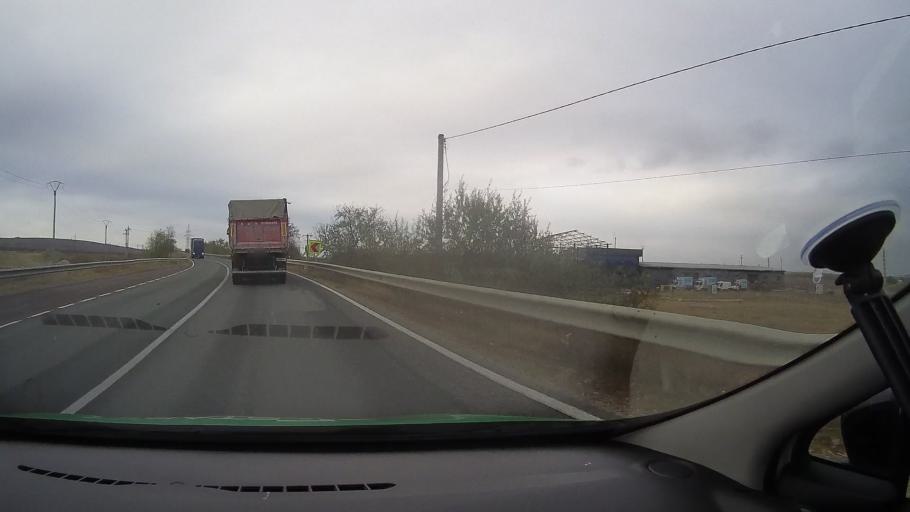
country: RO
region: Constanta
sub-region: Comuna Poarta Alba
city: Poarta Alba
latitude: 44.2137
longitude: 28.3935
